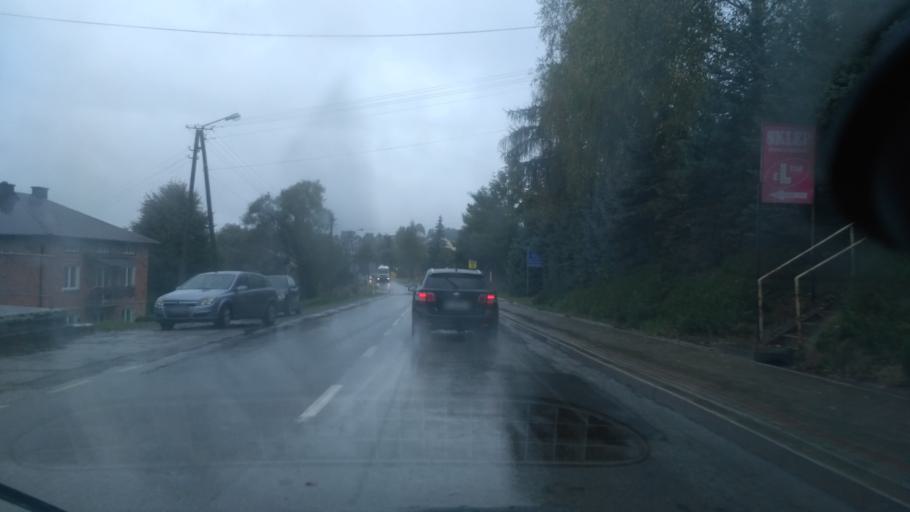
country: PL
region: Subcarpathian Voivodeship
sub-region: Powiat ropczycko-sedziszowski
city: Wielopole Skrzynskie
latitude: 49.9733
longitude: 21.5775
